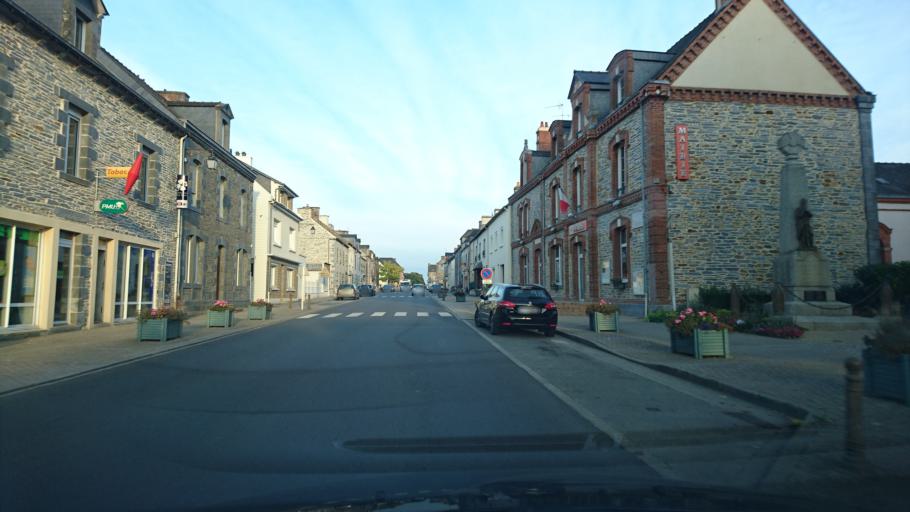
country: FR
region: Brittany
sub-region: Departement d'Ille-et-Vilaine
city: Sixt-sur-Aff
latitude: 47.7760
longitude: -2.0800
